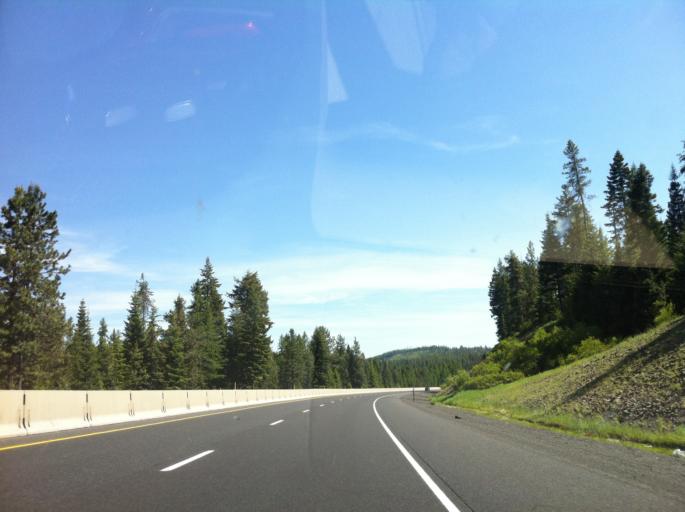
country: US
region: Oregon
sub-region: Union County
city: La Grande
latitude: 45.4738
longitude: -118.3961
